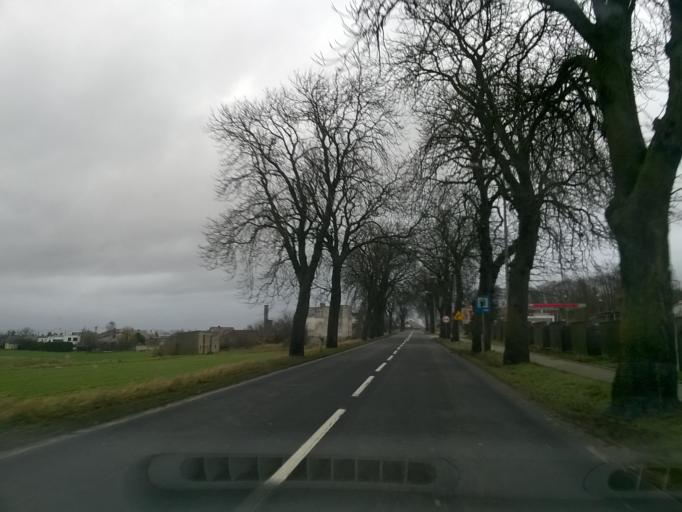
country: PL
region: Kujawsko-Pomorskie
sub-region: Powiat nakielski
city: Kcynia
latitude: 52.9894
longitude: 17.4768
